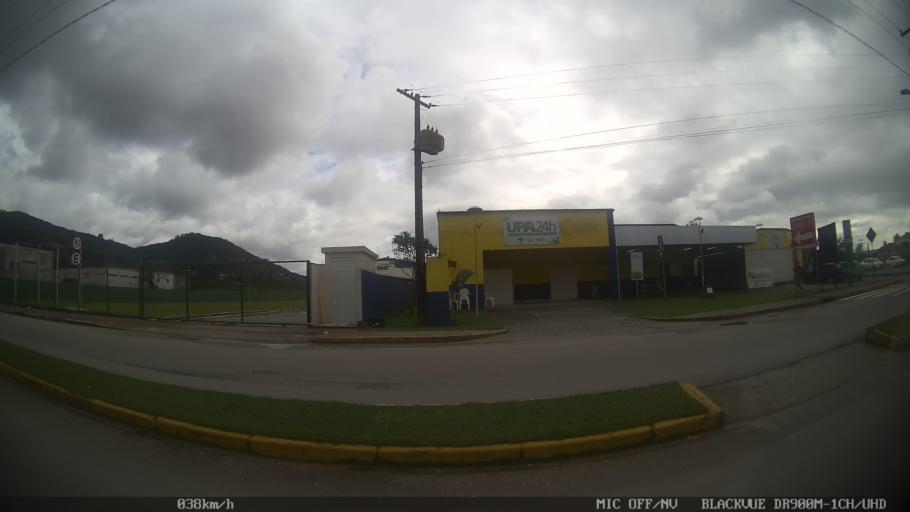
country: BR
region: Santa Catarina
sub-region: Biguacu
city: Biguacu
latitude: -27.5047
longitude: -48.6540
